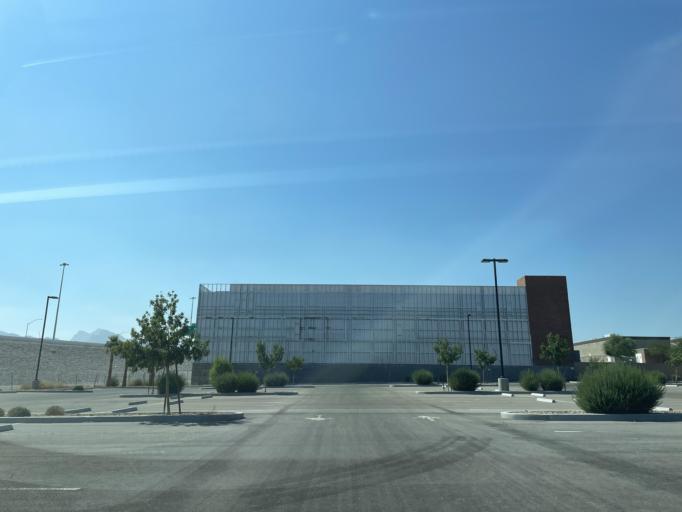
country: US
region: Nevada
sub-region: Clark County
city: Summerlin South
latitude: 36.2794
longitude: -115.2814
